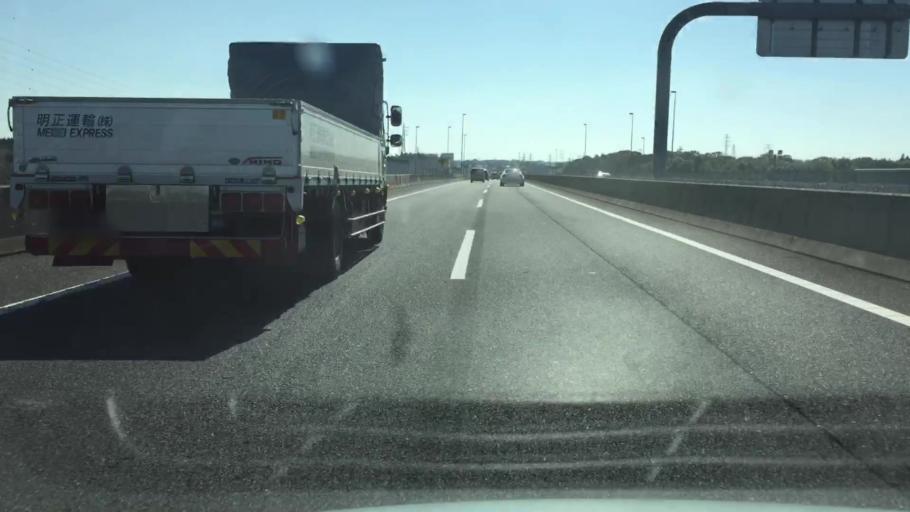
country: JP
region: Ibaraki
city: Naka
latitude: 36.0243
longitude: 140.1344
